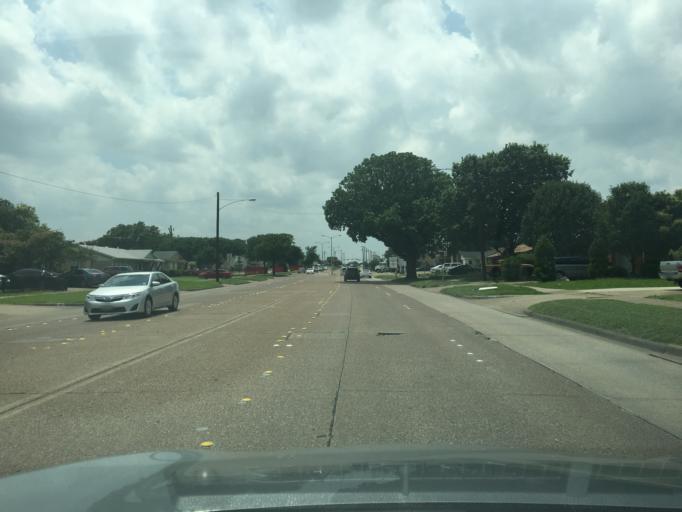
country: US
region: Texas
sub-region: Dallas County
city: Richardson
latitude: 32.9169
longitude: -96.6946
